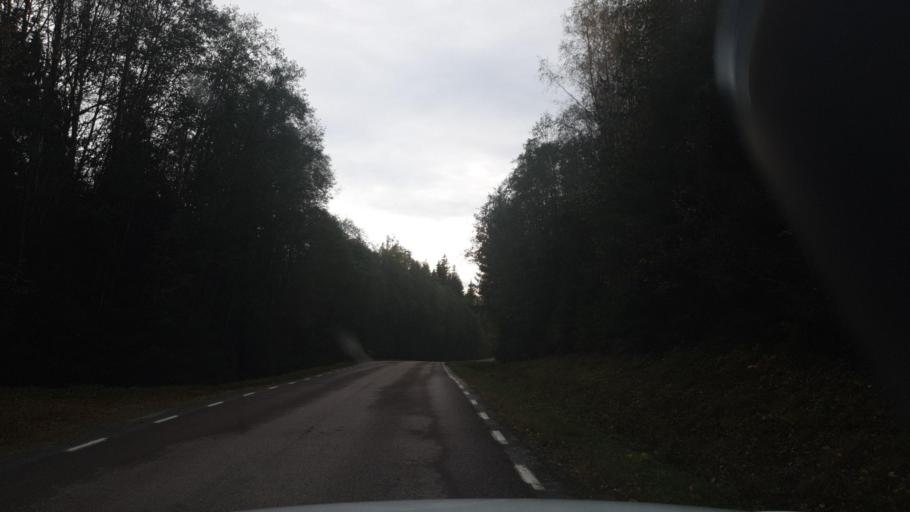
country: SE
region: Vaermland
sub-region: Arvika Kommun
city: Arvika
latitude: 59.6933
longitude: 12.7916
